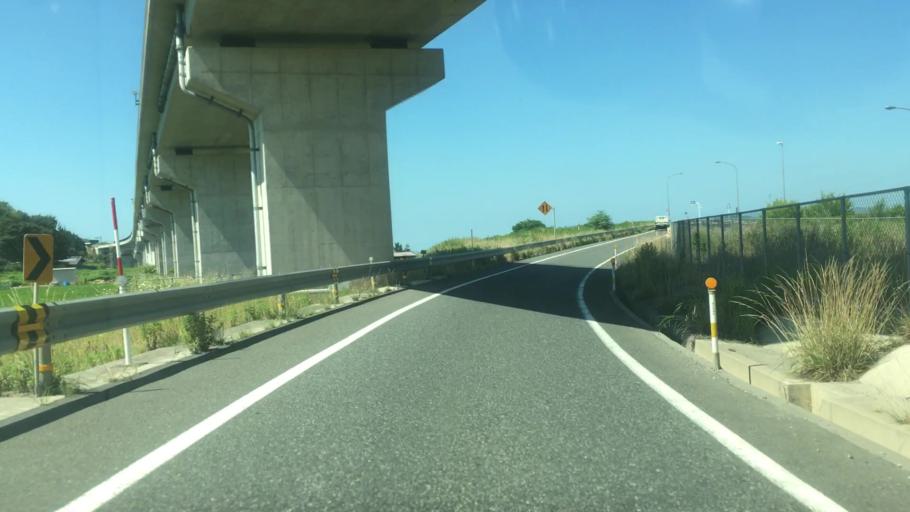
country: JP
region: Tottori
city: Tottori
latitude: 35.4348
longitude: 134.2045
